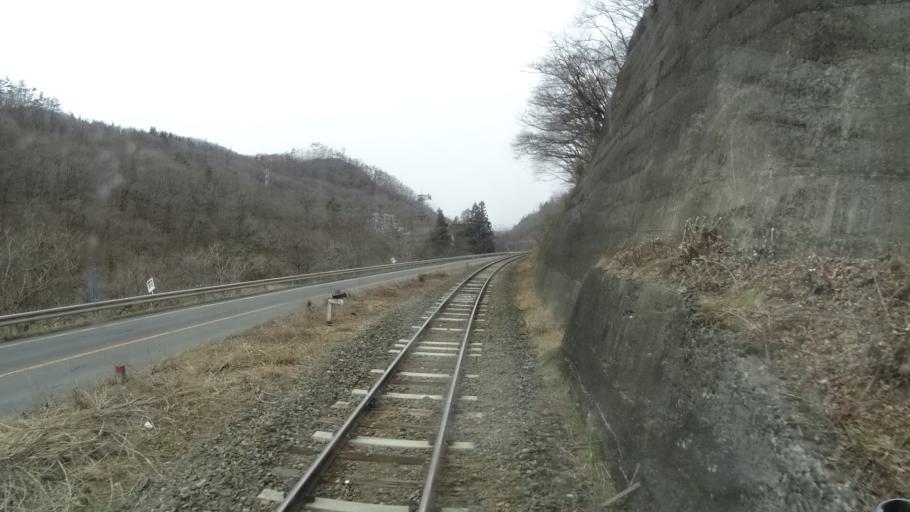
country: JP
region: Iwate
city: Hanamaki
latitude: 39.3612
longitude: 141.2897
